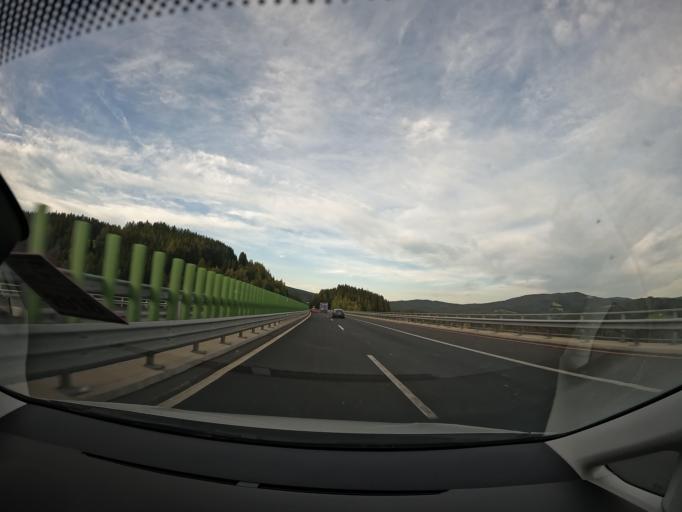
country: AT
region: Carinthia
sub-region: Politischer Bezirk Wolfsberg
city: Preitenegg
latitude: 46.9649
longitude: 14.9202
